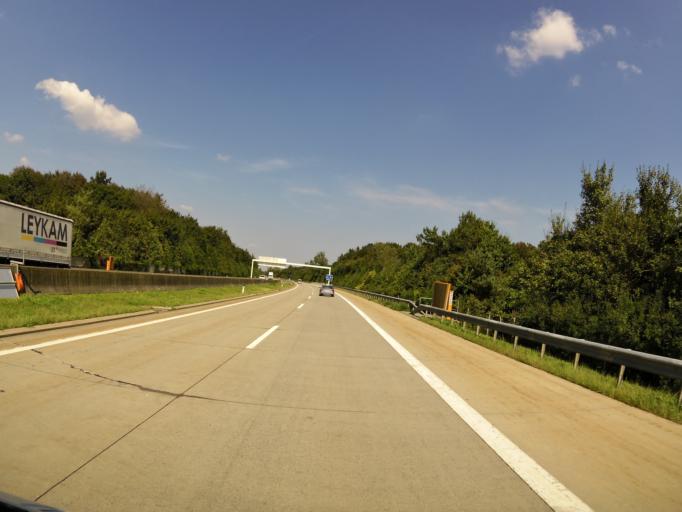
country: AT
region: Styria
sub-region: Politischer Bezirk Leibnitz
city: Spielfeld
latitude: 46.7139
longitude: 15.6463
